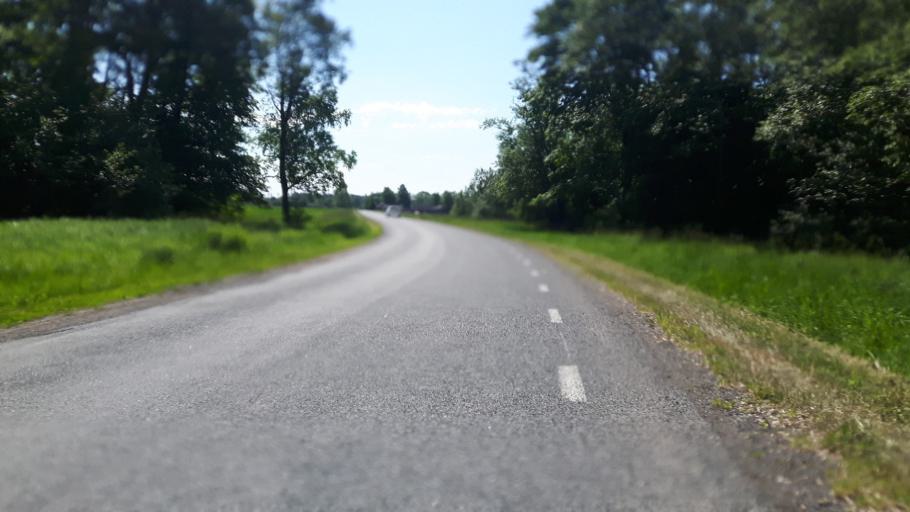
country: EE
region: Paernumaa
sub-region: Vaendra vald (alev)
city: Vandra
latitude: 58.5984
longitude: 25.0218
